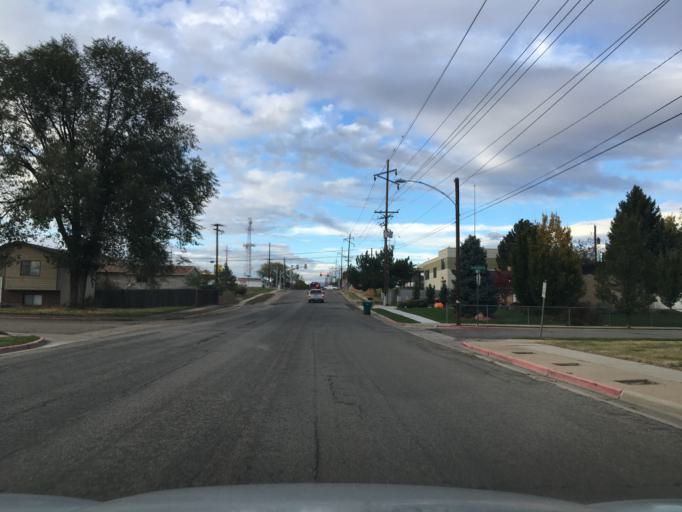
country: US
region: Utah
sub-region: Davis County
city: Layton
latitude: 41.0776
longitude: -111.9879
